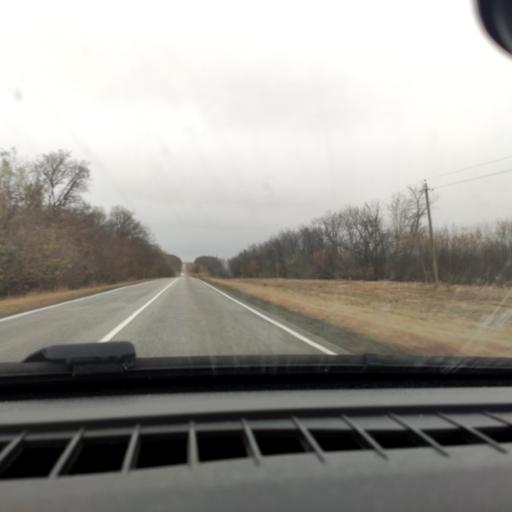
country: RU
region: Voronezj
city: Uryv-Pokrovka
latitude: 51.0994
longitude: 39.0148
